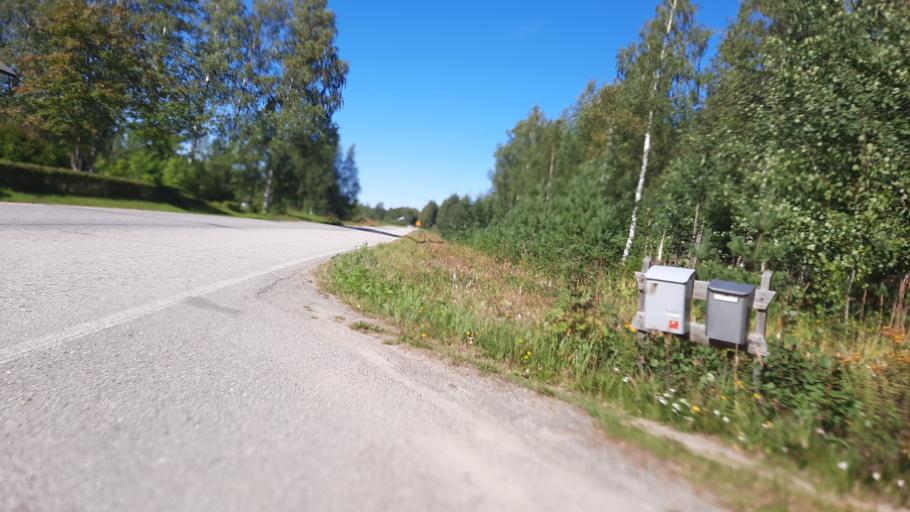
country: FI
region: North Karelia
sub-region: Joensuu
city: Joensuu
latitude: 62.6308
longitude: 29.7343
